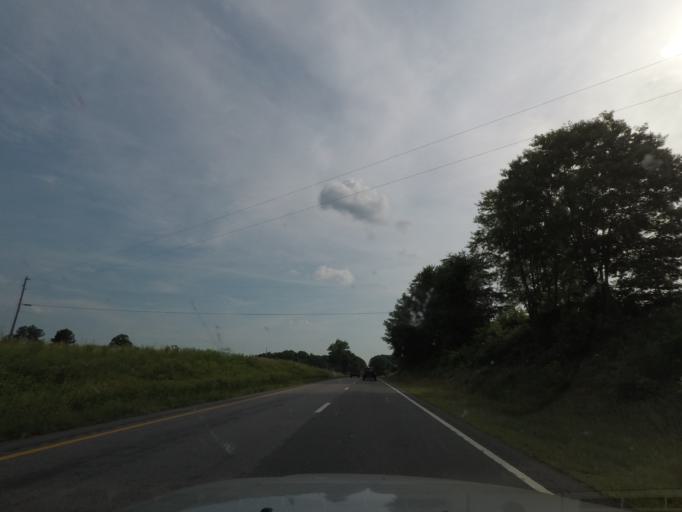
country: US
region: Virginia
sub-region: Mecklenburg County
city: Chase City
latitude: 36.8865
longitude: -78.5537
